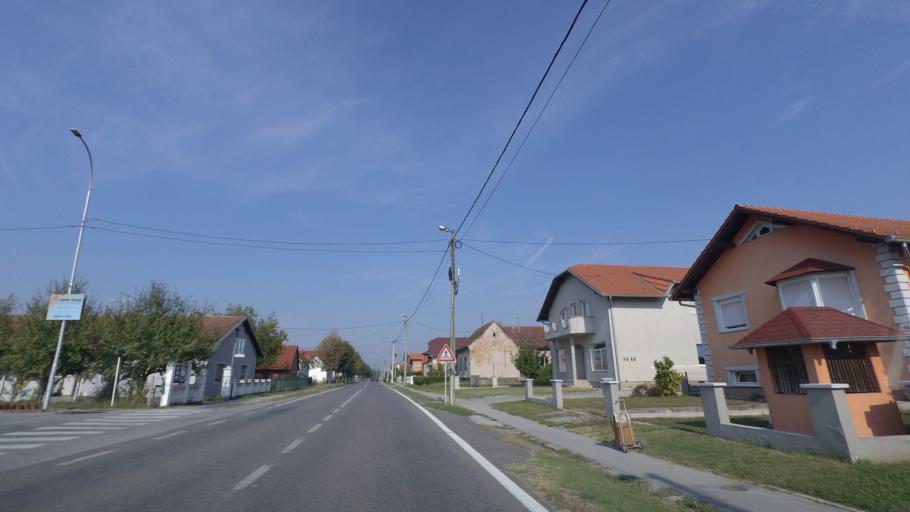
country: HR
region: Pozesko-Slavonska
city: Lipik
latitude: 45.4150
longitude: 17.1538
